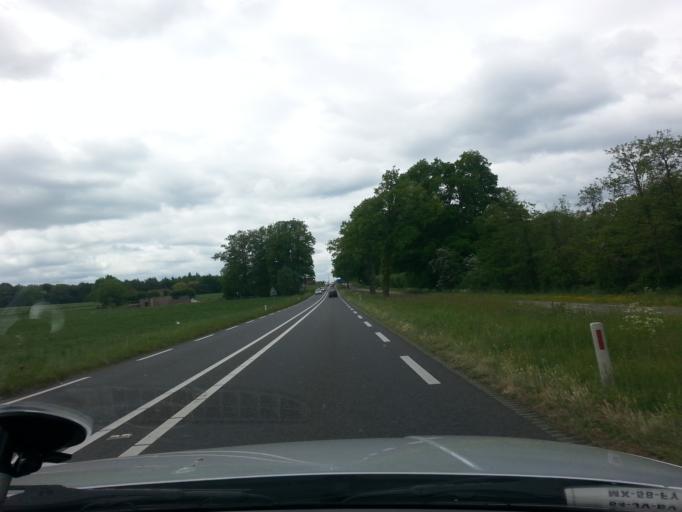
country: NL
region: Overijssel
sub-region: Gemeente Oldenzaal
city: Oldenzaal
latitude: 52.3260
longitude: 6.9451
